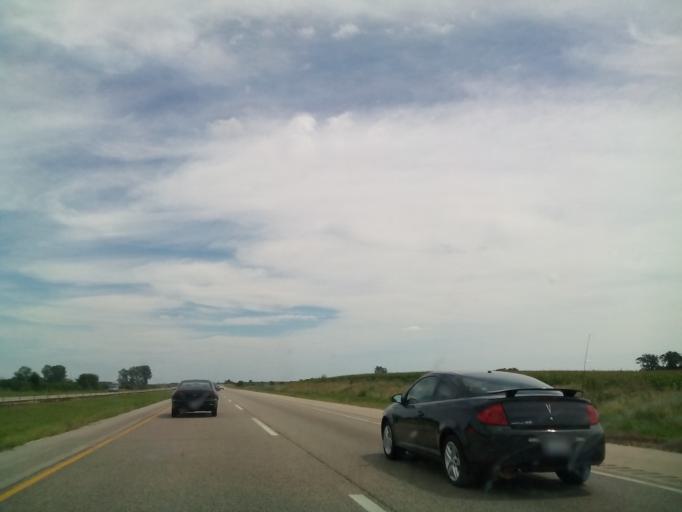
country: US
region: Illinois
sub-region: Kane County
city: Maple Park
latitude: 41.8641
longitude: -88.5610
